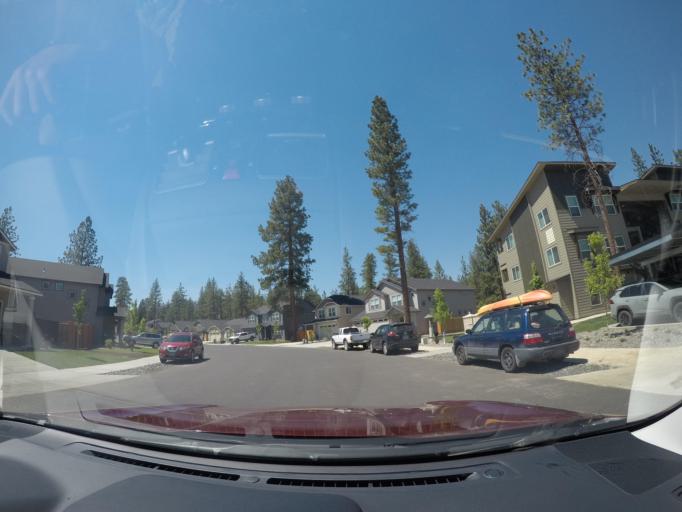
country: US
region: Oregon
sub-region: Deschutes County
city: Sisters
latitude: 44.2980
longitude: -121.5649
